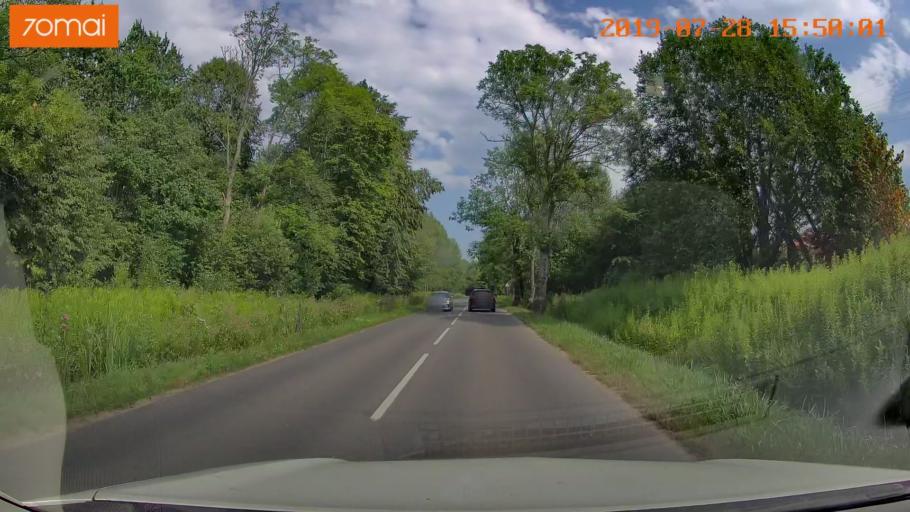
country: RU
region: Kaliningrad
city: Otradnoye
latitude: 54.9399
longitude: 20.0854
